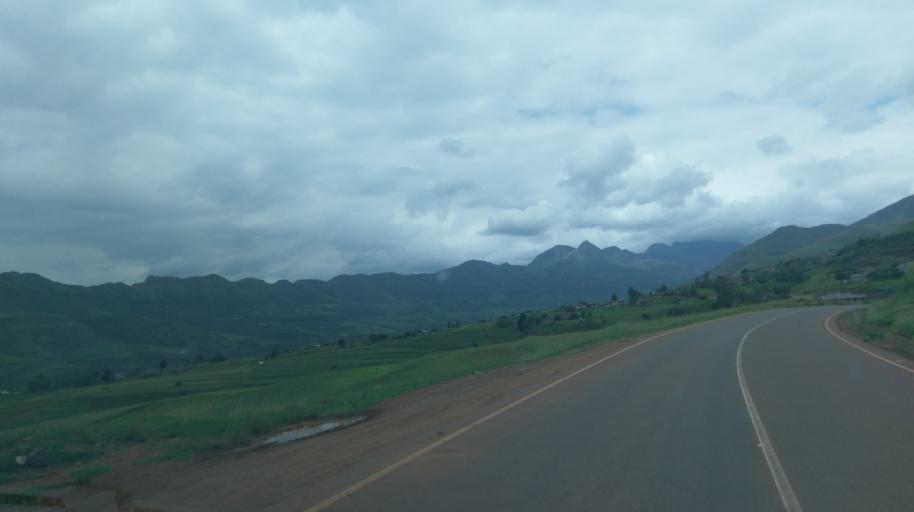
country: LS
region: Butha-Buthe
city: Butha-Buthe
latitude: -29.0327
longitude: 28.2596
